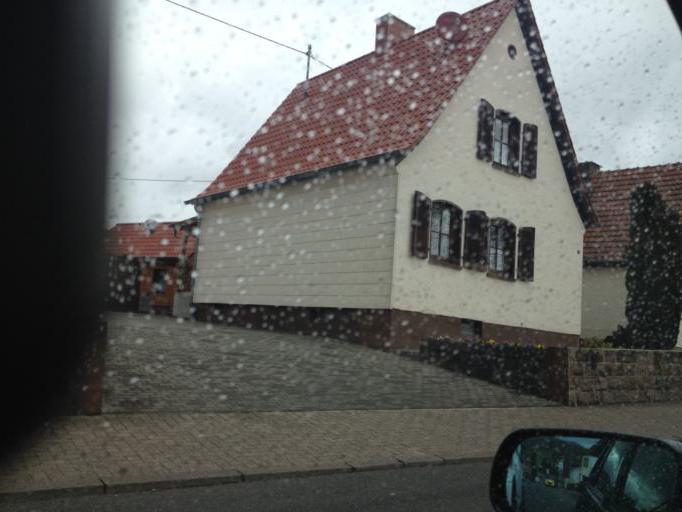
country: DE
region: Saarland
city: Bexbach
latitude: 49.3242
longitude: 7.2192
